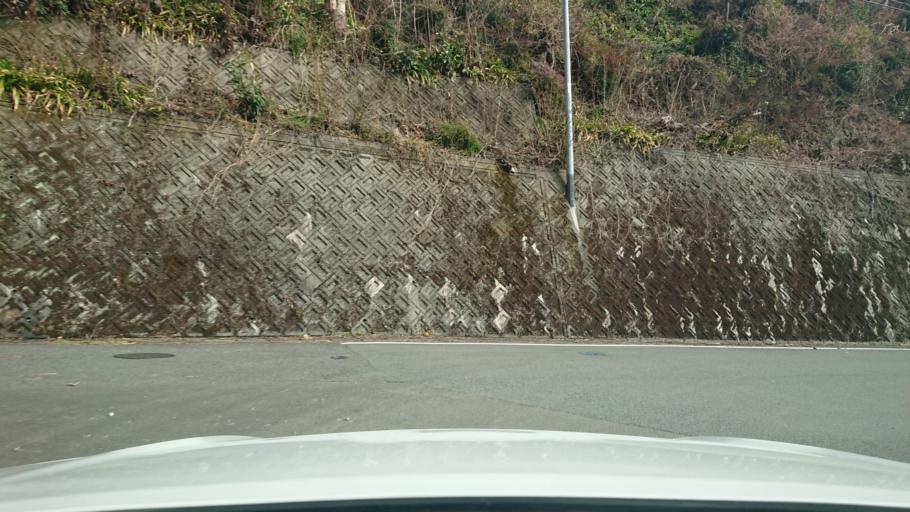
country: JP
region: Tokushima
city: Ishii
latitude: 33.9150
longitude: 134.4059
